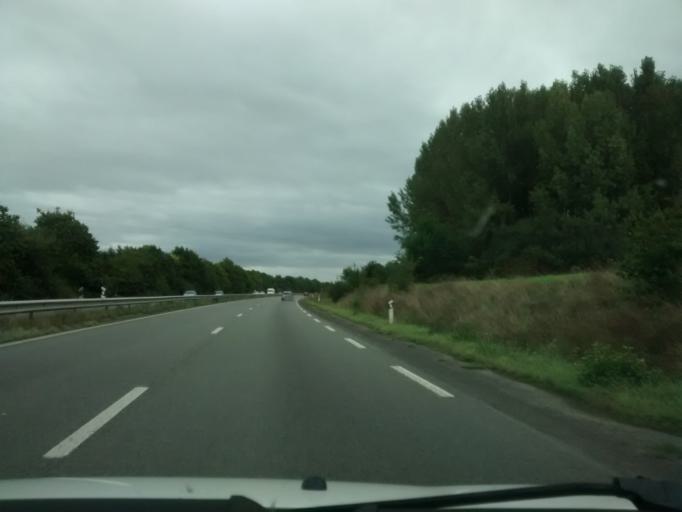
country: FR
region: Brittany
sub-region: Departement d'Ille-et-Vilaine
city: Vignoc
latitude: 48.2707
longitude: -1.7836
